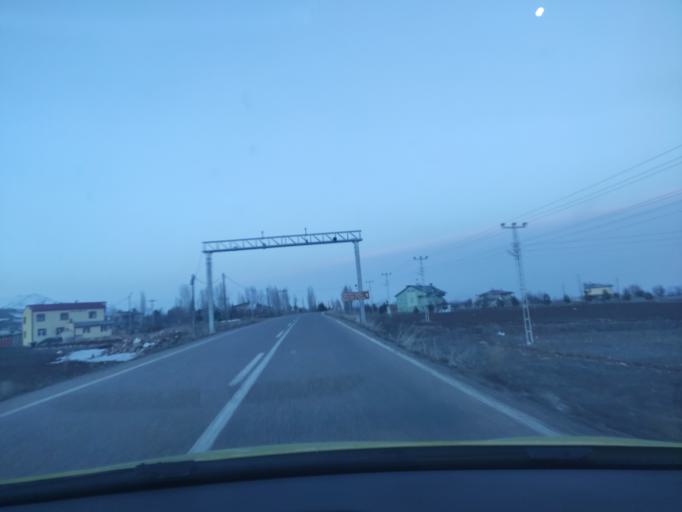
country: TR
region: Bayburt
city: Aydintepe
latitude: 40.3833
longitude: 40.1278
